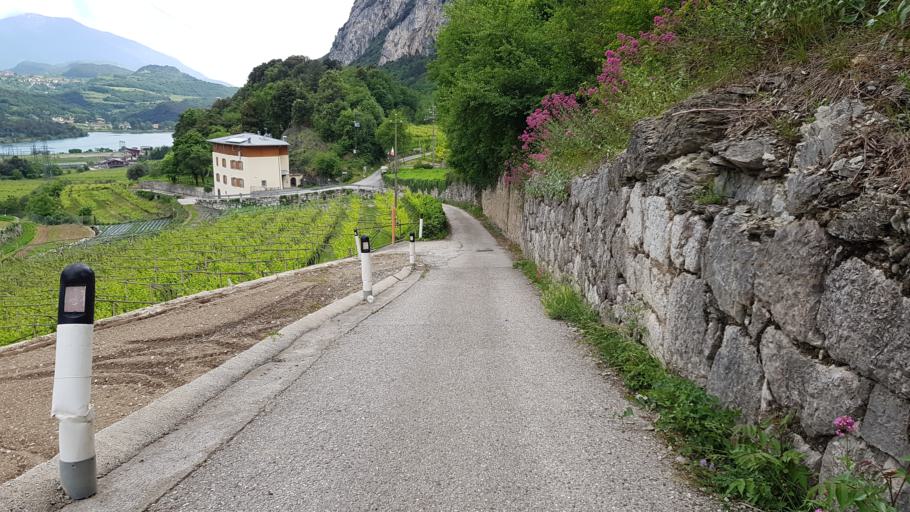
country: IT
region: Trentino-Alto Adige
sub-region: Provincia di Trento
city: Vezzano
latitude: 46.0764
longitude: 10.9860
